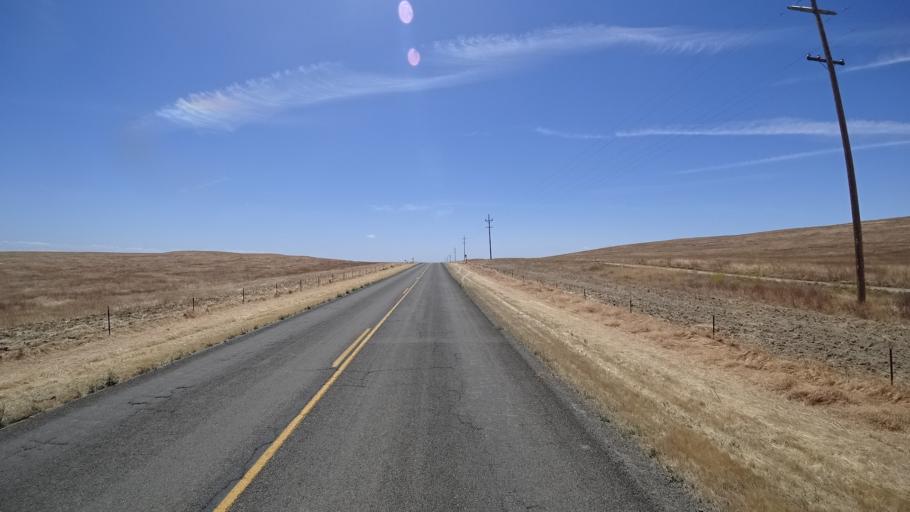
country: US
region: California
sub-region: Kings County
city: Kettleman City
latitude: 35.8710
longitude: -119.9153
